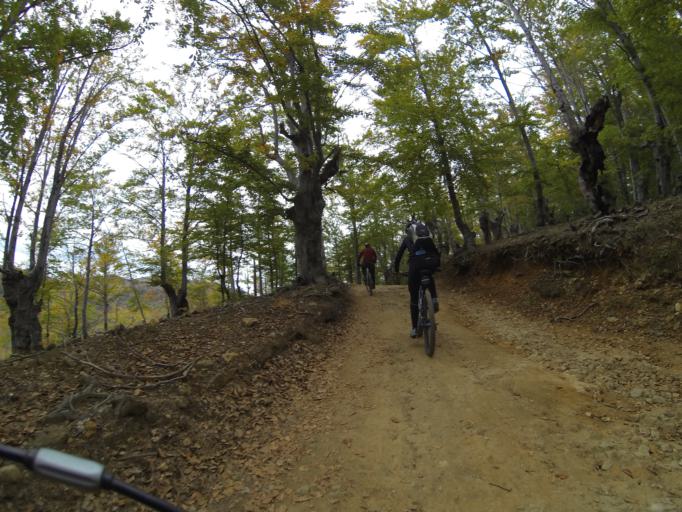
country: RO
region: Gorj
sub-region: Comuna Tismana
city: Sohodol
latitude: 45.0711
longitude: 22.8619
